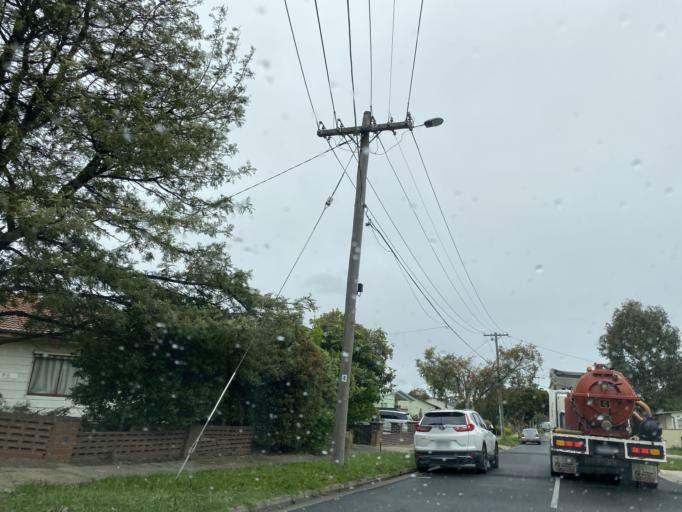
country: AU
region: Victoria
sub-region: Moreland
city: Fawkner
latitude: -37.7119
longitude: 144.9722
